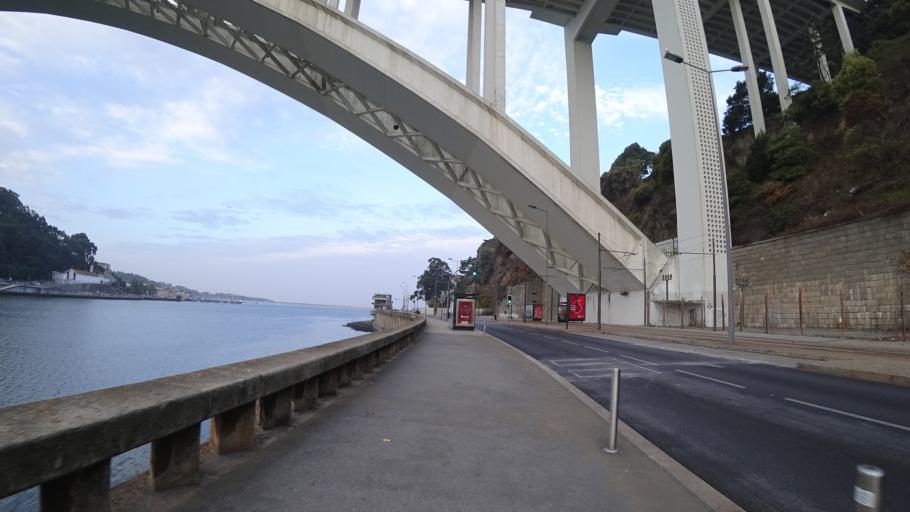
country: PT
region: Porto
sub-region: Vila Nova de Gaia
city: Canidelo
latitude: 41.1484
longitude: -8.6400
